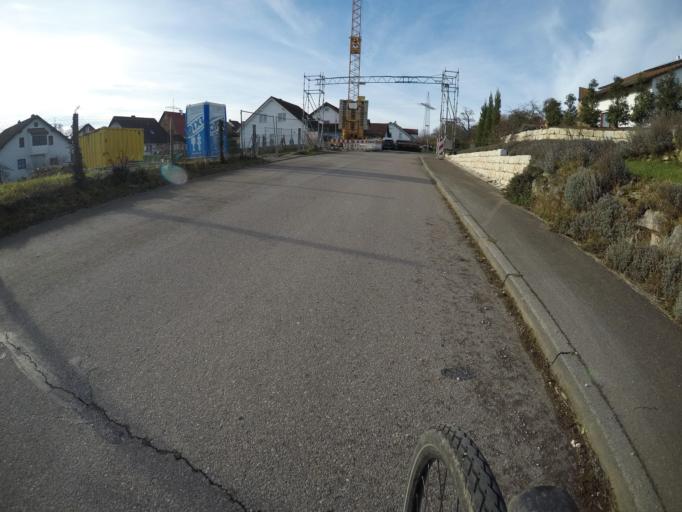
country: DE
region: Baden-Wuerttemberg
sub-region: Regierungsbezirk Stuttgart
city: Dettingen unter Teck
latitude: 48.6191
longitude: 9.4468
